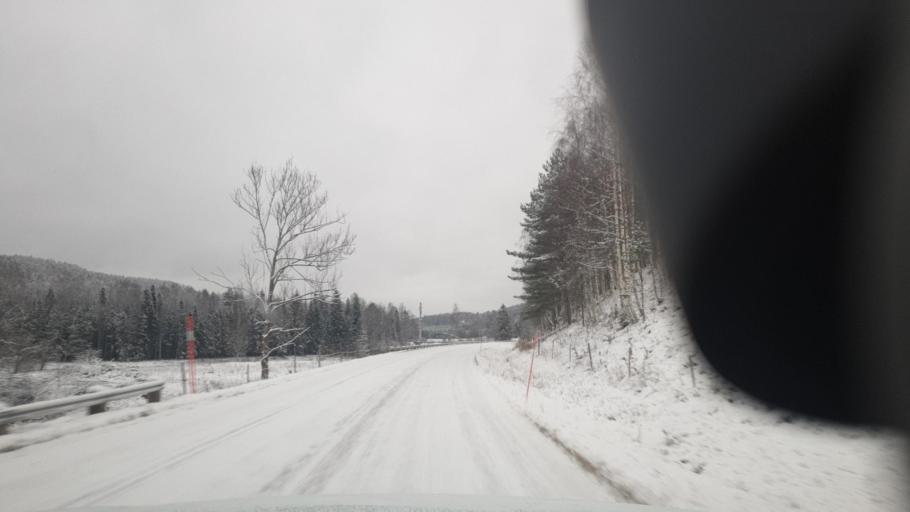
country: NO
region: Hedmark
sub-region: Eidskog
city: Skotterud
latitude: 59.7779
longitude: 12.0459
